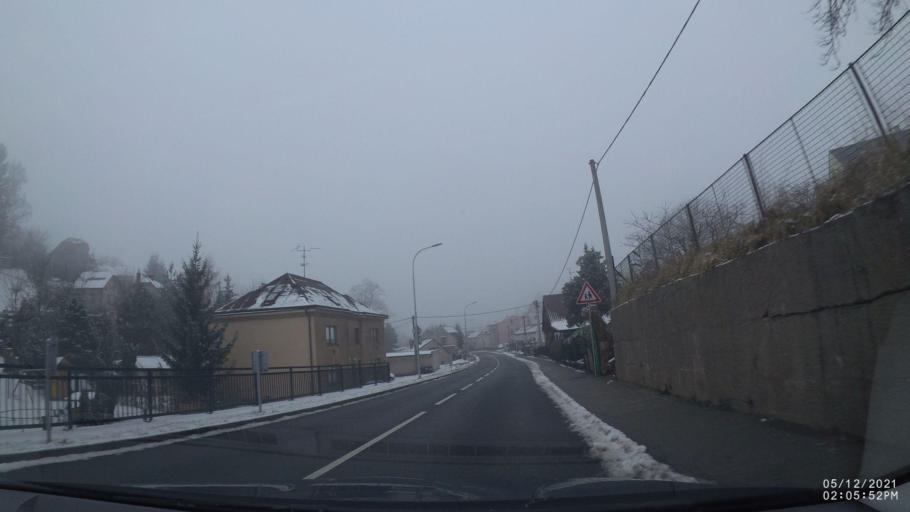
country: CZ
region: Kralovehradecky
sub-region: Okres Nachod
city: Cerveny Kostelec
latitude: 50.4862
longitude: 16.1074
